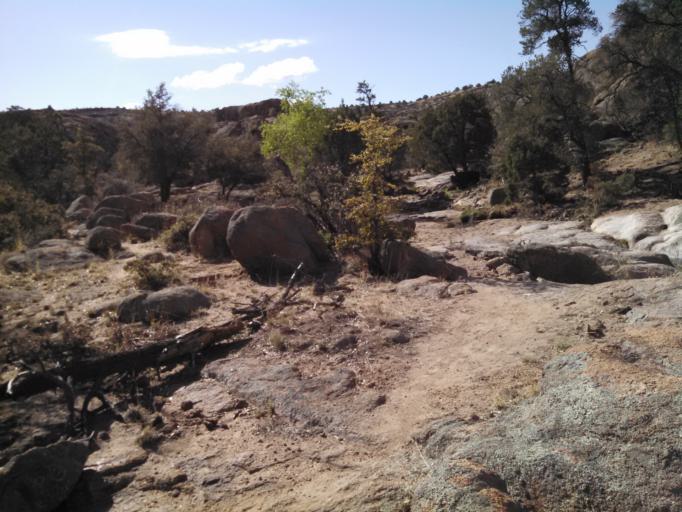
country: US
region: Arizona
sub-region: Yavapai County
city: Prescott
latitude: 34.5924
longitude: -112.4037
